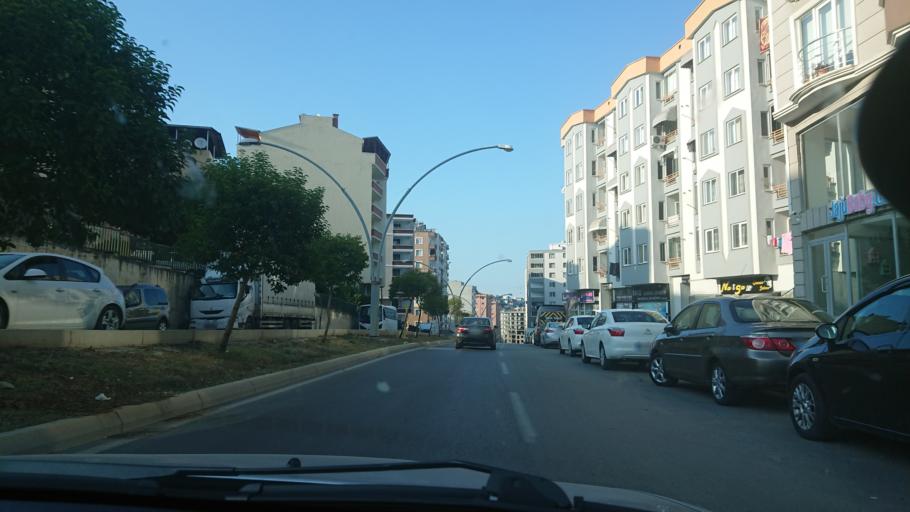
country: TR
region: Samsun
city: Samsun
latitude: 41.2976
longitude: 36.3236
